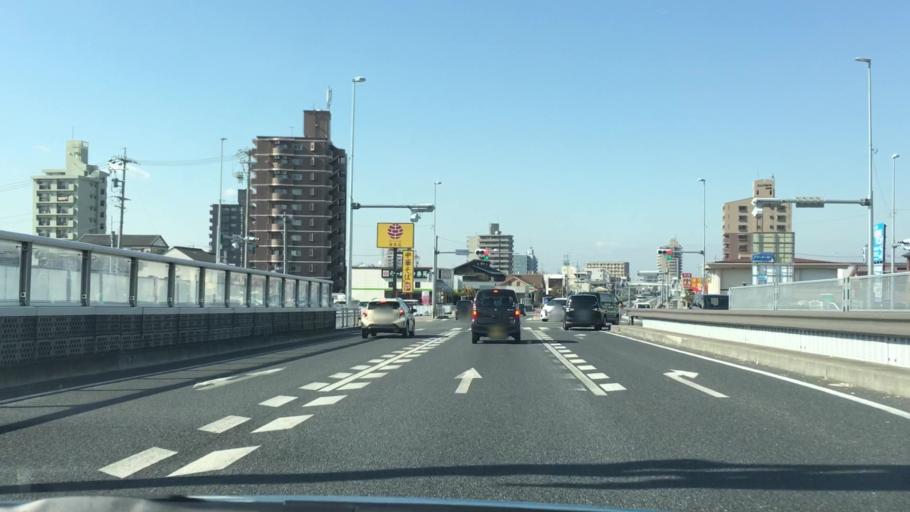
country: JP
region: Aichi
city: Okazaki
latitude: 34.9603
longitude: 137.1460
